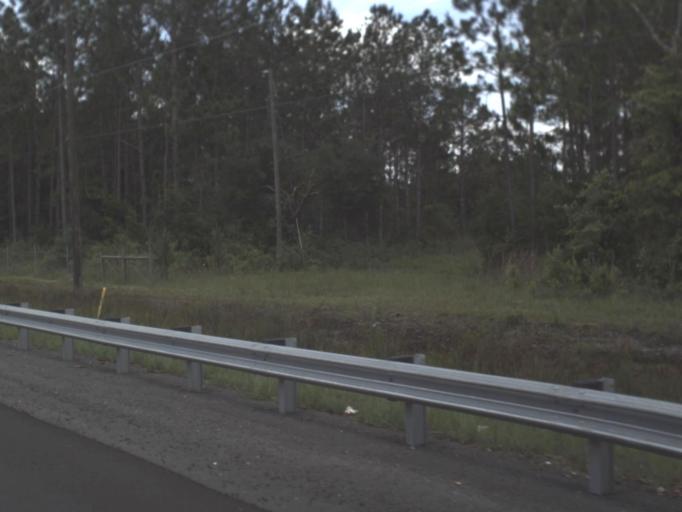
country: US
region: Florida
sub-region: Duval County
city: Baldwin
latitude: 30.4219
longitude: -81.9269
